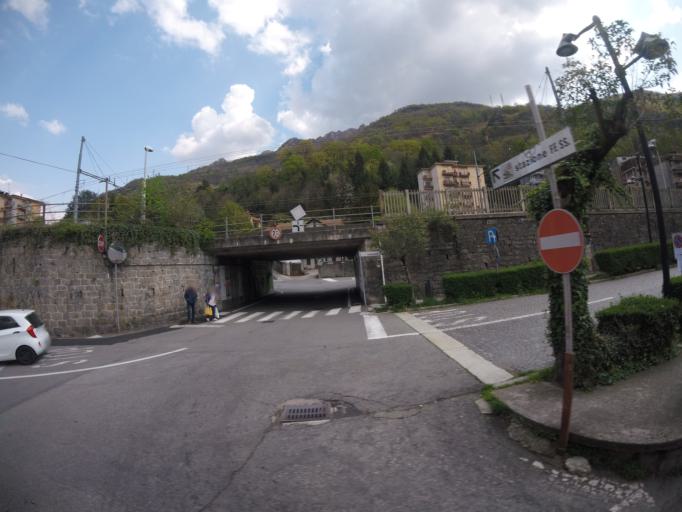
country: IT
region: Piedmont
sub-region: Provincia Verbano-Cusio-Ossola
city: Omegna
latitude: 45.8731
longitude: 8.4128
